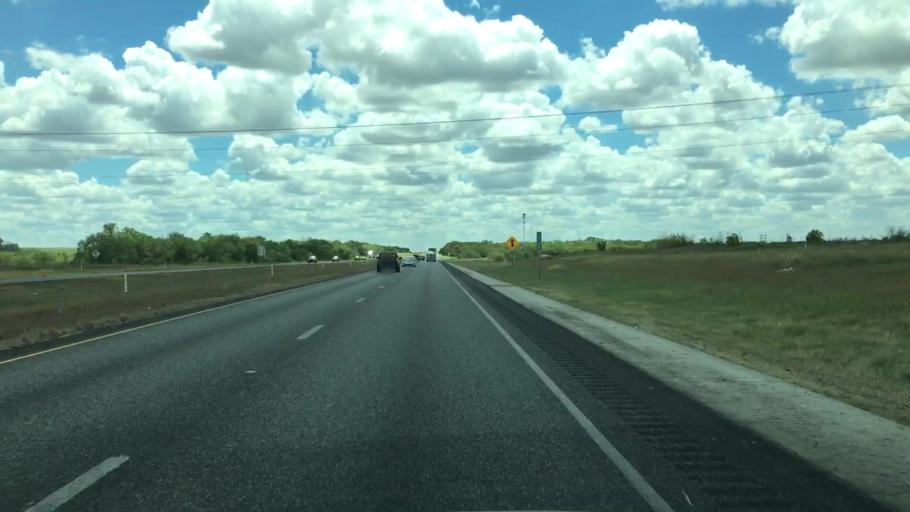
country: US
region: Texas
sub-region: Bexar County
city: Elmendorf
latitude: 29.1415
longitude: -98.4290
